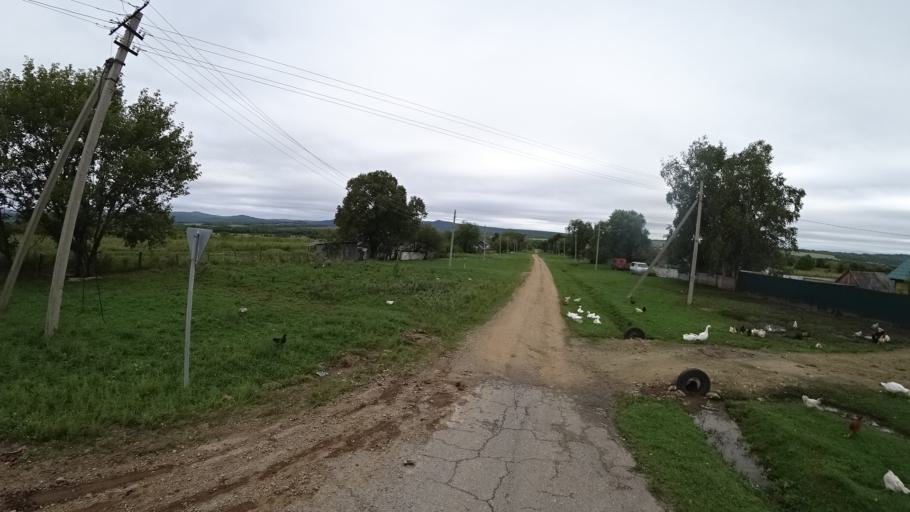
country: RU
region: Primorskiy
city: Rettikhovka
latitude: 44.1398
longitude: 132.6513
